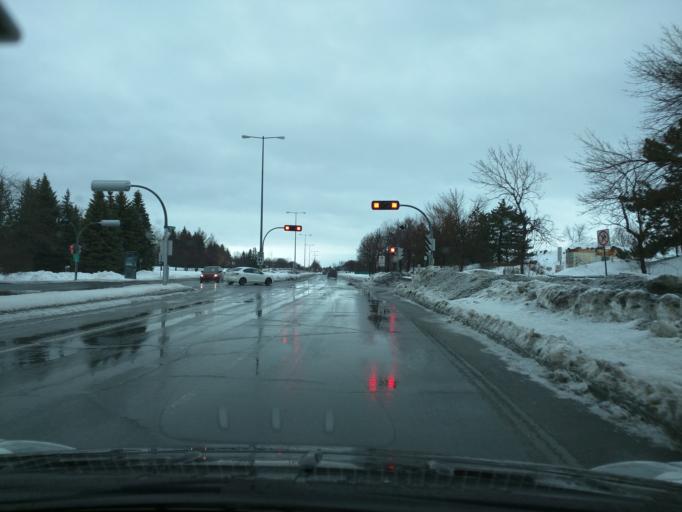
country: CA
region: Quebec
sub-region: Monteregie
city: Longueuil
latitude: 45.5085
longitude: -73.4712
